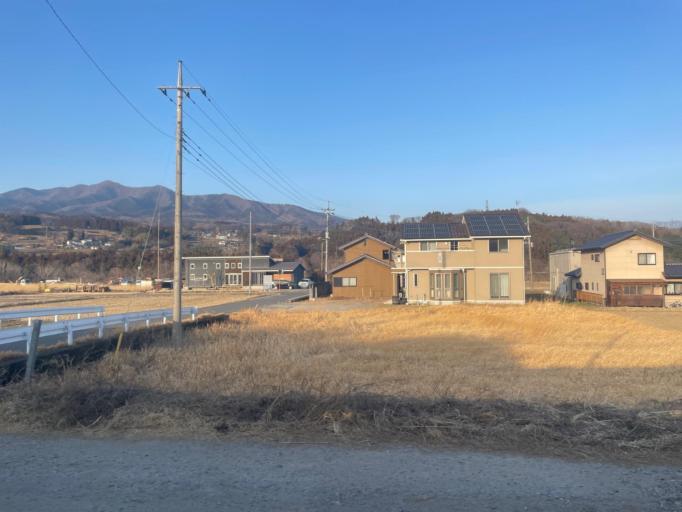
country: JP
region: Gunma
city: Shibukawa
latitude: 36.5311
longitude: 138.9743
